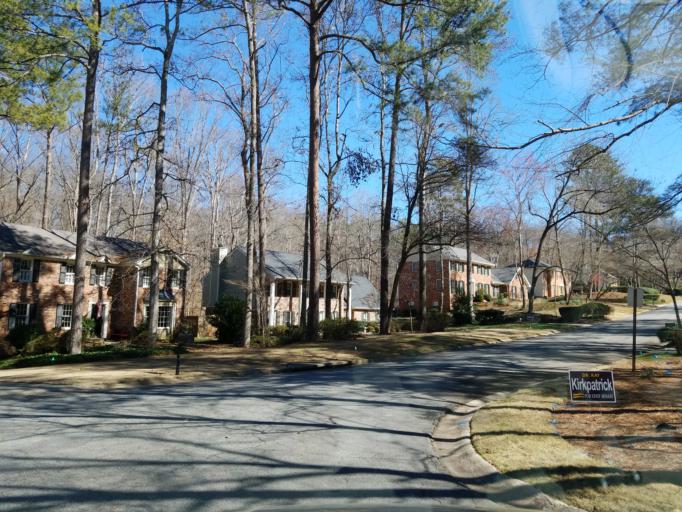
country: US
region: Georgia
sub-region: Fulton County
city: Sandy Springs
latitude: 33.9748
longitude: -84.4507
